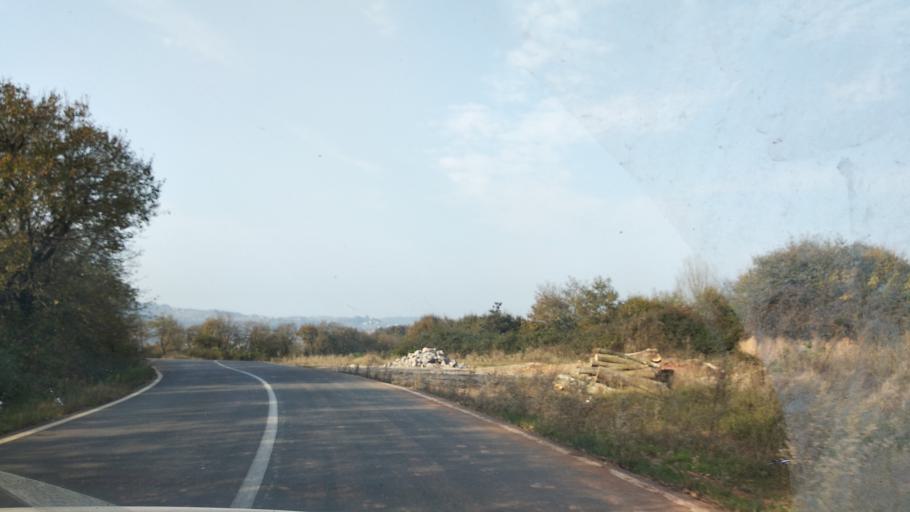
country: TR
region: Sakarya
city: Karasu
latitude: 41.0659
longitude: 30.6171
